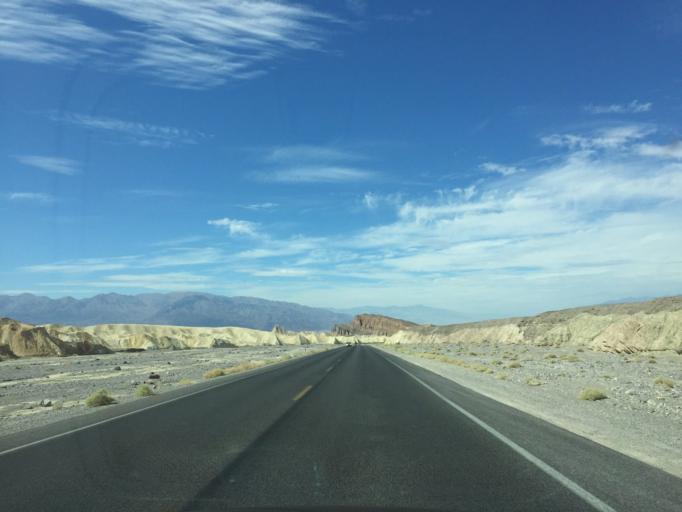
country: US
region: Nevada
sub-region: Nye County
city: Beatty
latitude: 36.4110
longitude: -116.7969
